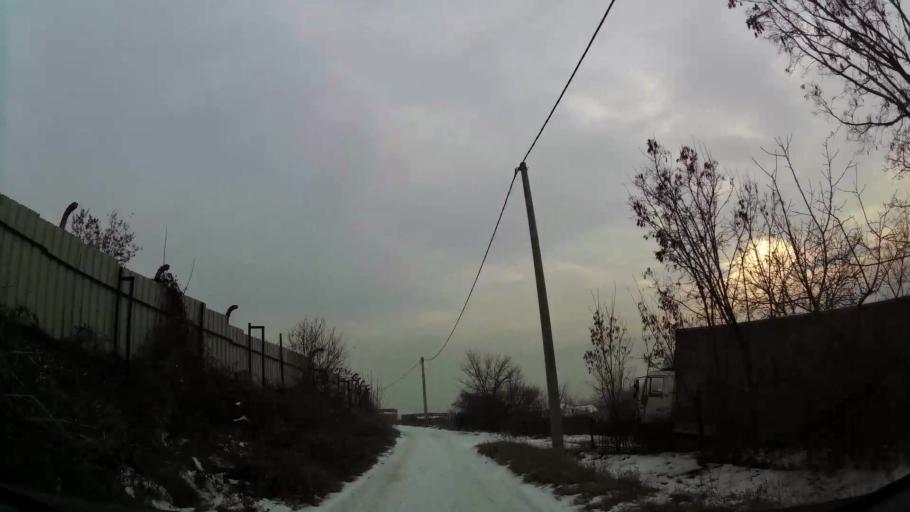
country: MK
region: Suto Orizari
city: Suto Orizare
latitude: 42.0392
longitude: 21.4310
